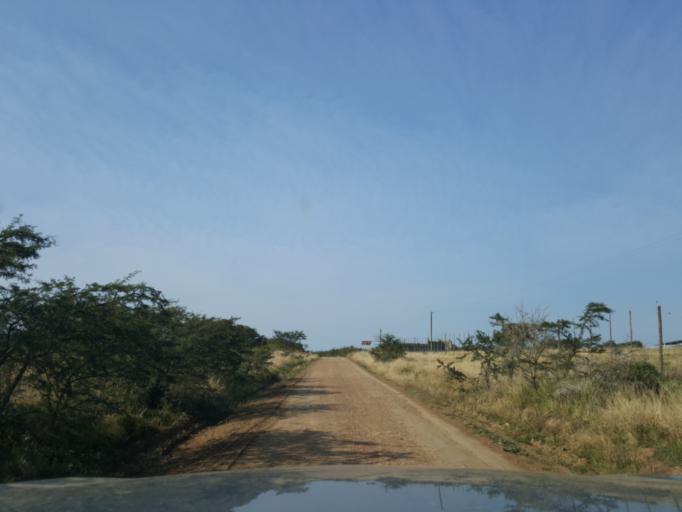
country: ZA
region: Eastern Cape
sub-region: Cacadu District Municipality
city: Grahamstown
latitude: -33.4079
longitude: 26.2988
